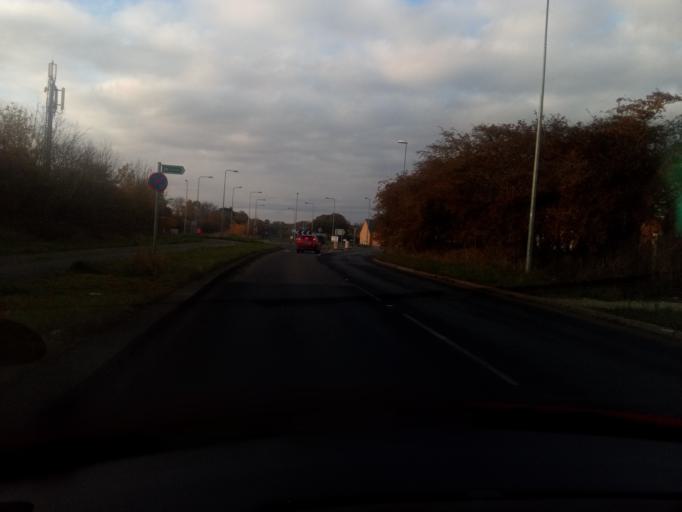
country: GB
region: England
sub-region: City and Borough of Leeds
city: Wetherby
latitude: 53.9386
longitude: -1.3781
